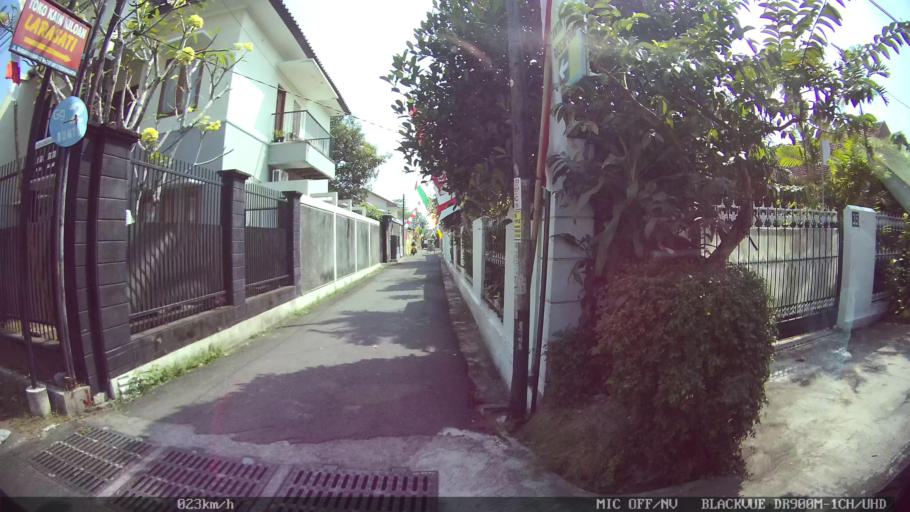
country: ID
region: Daerah Istimewa Yogyakarta
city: Yogyakarta
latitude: -7.8111
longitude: 110.3847
